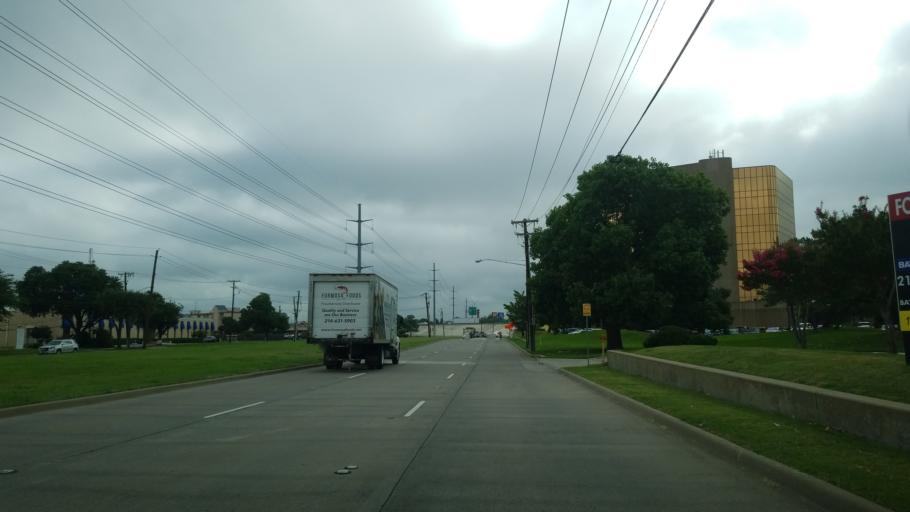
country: US
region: Texas
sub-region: Dallas County
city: Irving
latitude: 32.8339
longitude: -96.8779
